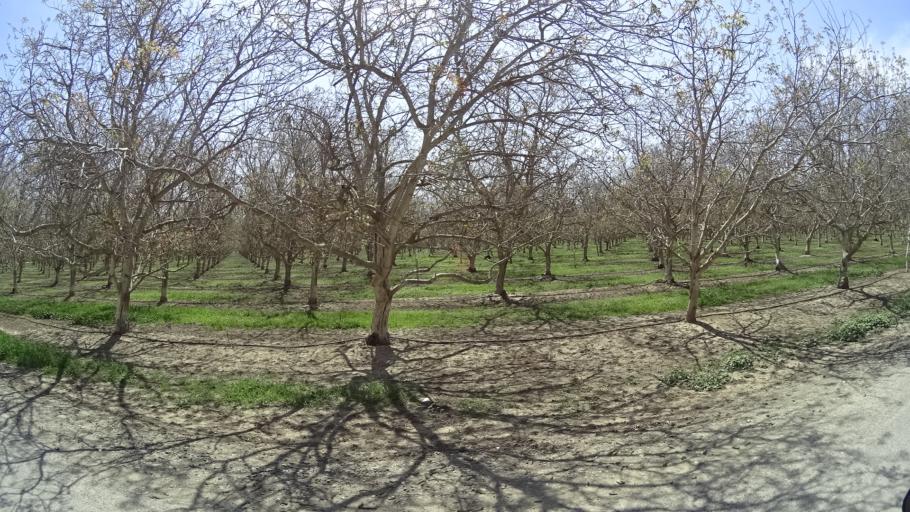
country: US
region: California
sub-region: Glenn County
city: Willows
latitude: 39.5037
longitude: -122.0158
